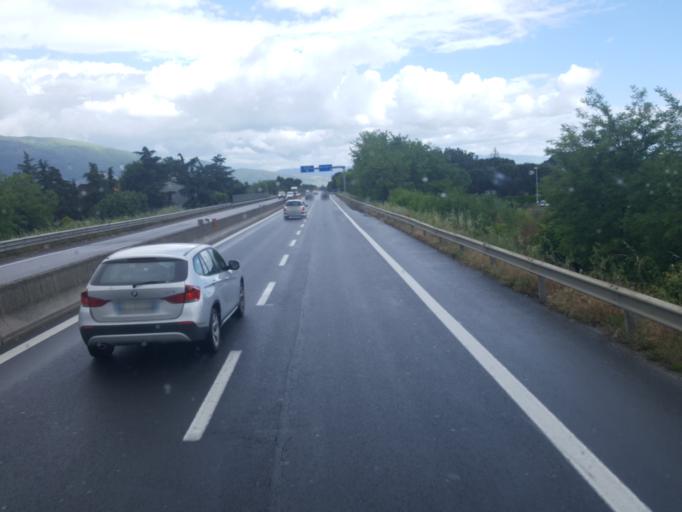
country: IT
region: Umbria
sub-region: Provincia di Perugia
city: Bastia umbra
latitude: 43.0681
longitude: 12.5337
